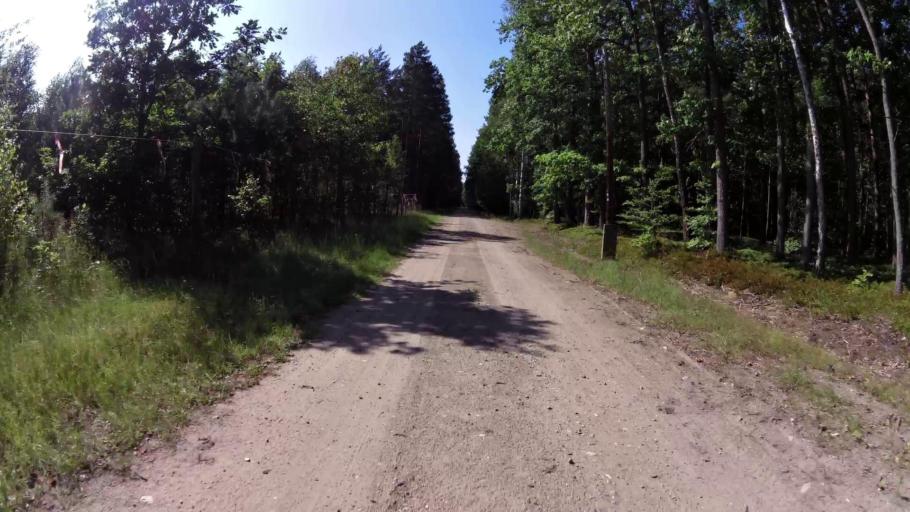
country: PL
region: West Pomeranian Voivodeship
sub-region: Powiat drawski
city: Czaplinek
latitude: 53.4109
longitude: 16.2545
